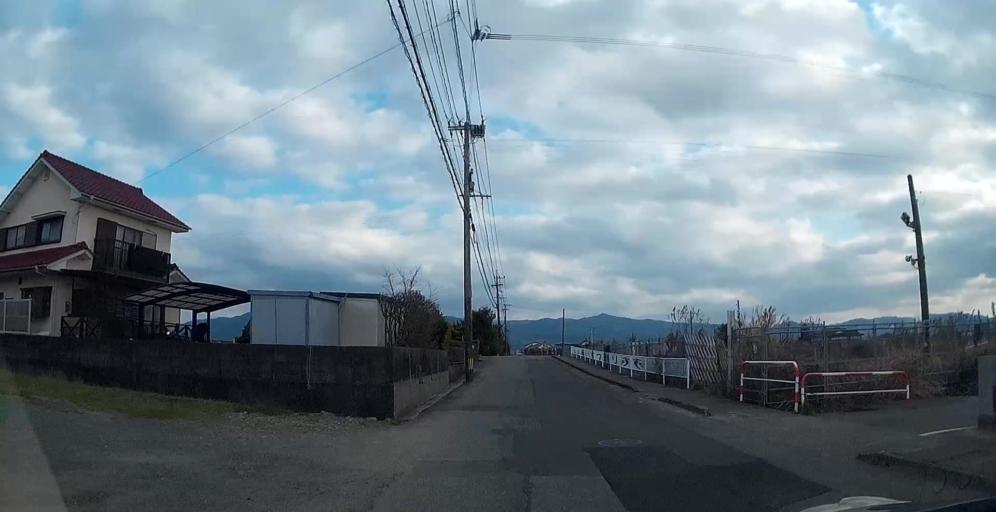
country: JP
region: Kumamoto
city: Yatsushiro
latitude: 32.5477
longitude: 130.6158
